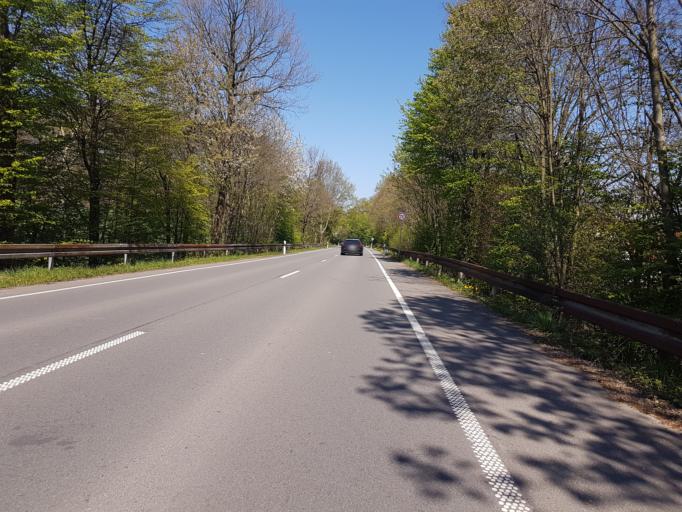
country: DE
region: North Rhine-Westphalia
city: Gevelsberg
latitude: 51.3629
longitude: 7.3289
